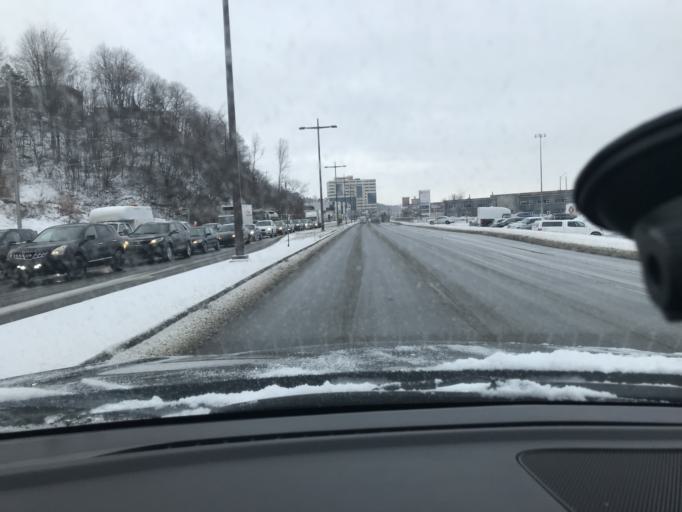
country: CA
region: Quebec
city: Quebec
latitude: 46.8021
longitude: -71.2488
